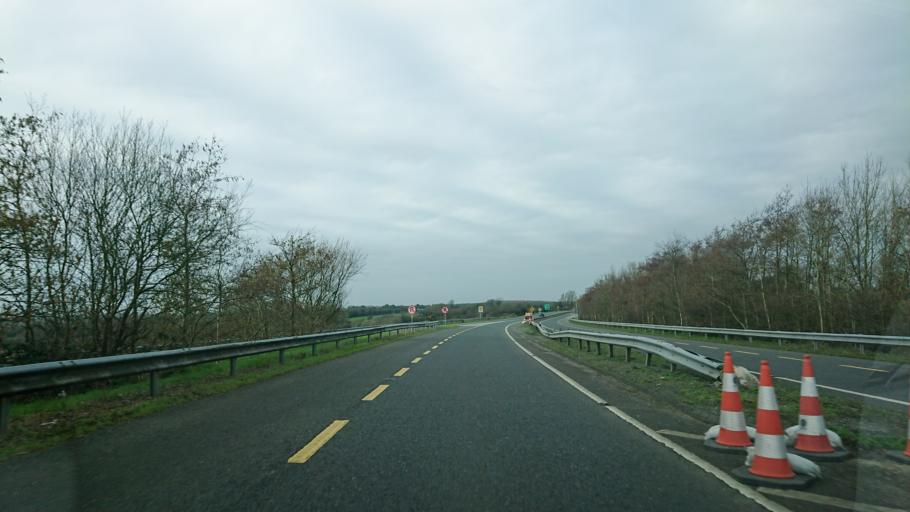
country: IE
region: Munster
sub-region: County Cork
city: Youghal
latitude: 51.9401
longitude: -7.9008
